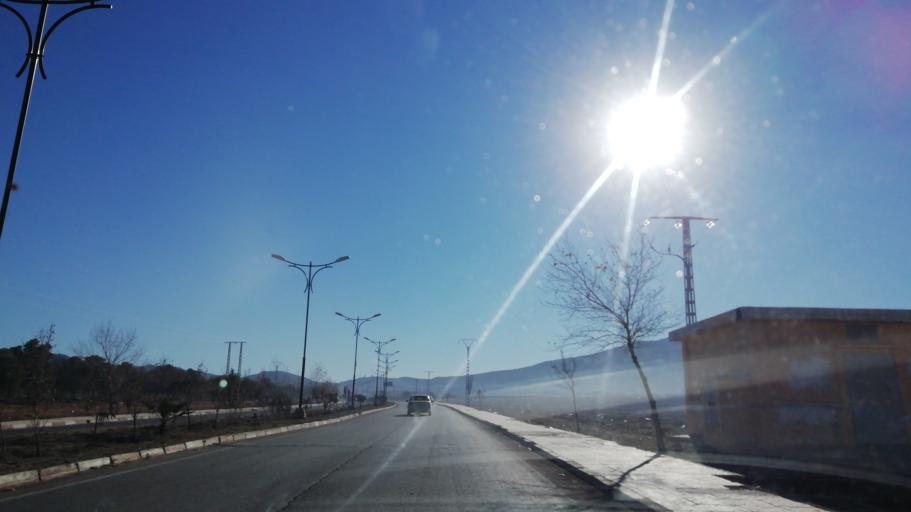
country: DZ
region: El Bayadh
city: El Bayadh
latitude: 33.6632
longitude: 1.0521
